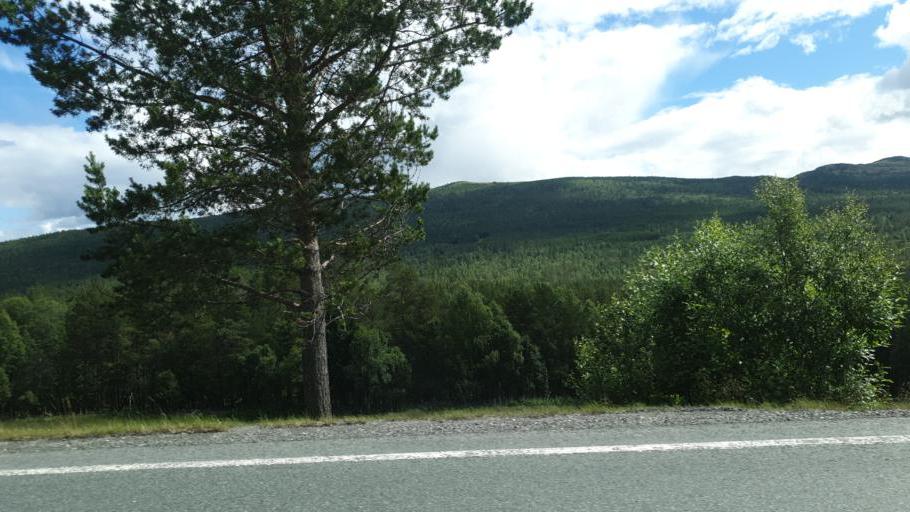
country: NO
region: Sor-Trondelag
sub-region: Rennebu
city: Berkak
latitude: 62.6730
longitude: 9.9117
